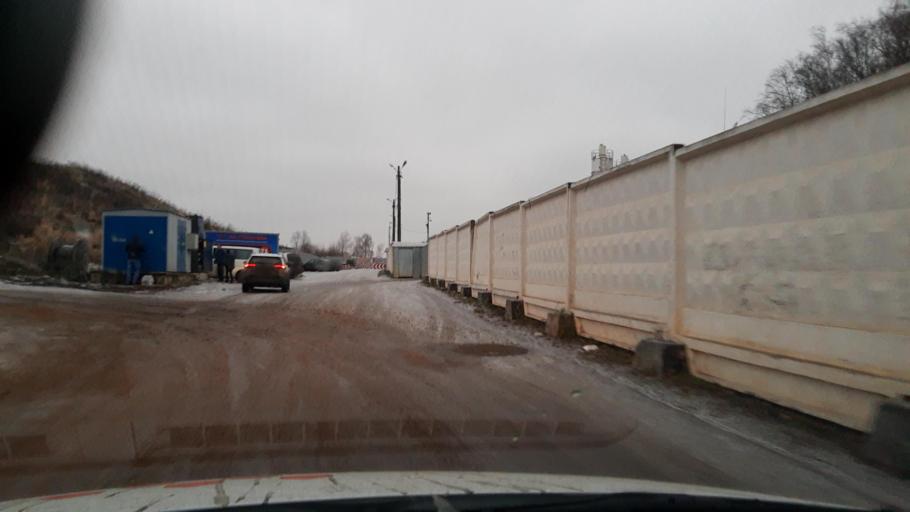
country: RU
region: Moscow
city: Solntsevo
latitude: 55.6227
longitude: 37.3863
